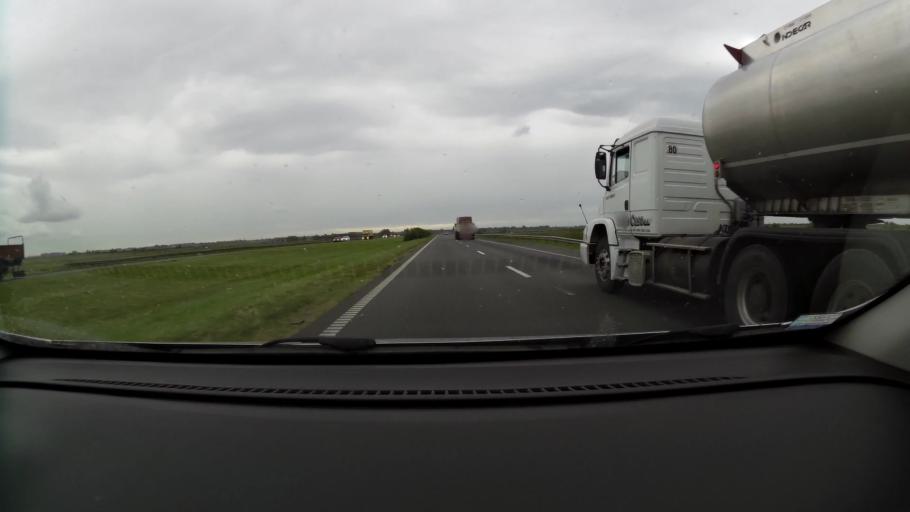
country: AR
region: Buenos Aires
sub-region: Partido de Baradero
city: Baradero
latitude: -33.8160
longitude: -59.5952
